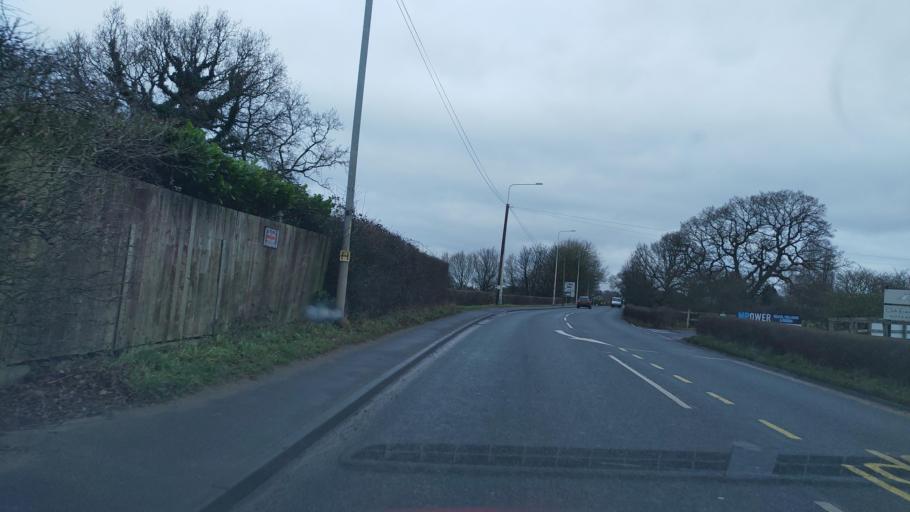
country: GB
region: England
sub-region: Lancashire
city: Clayton-le-Woods
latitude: 53.7031
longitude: -2.6731
